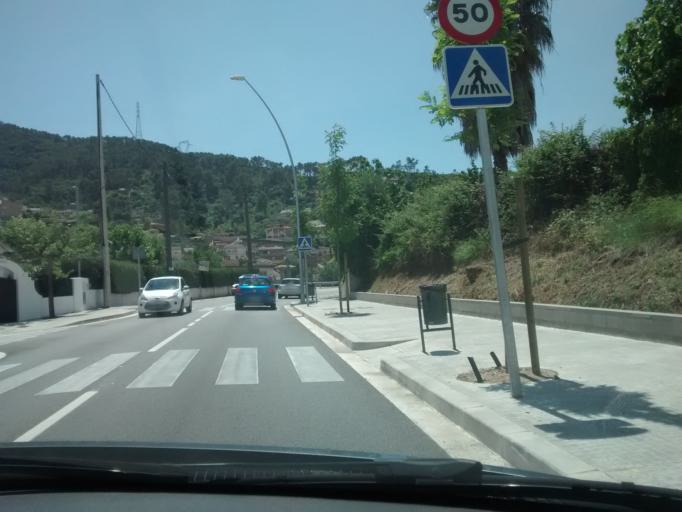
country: ES
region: Catalonia
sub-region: Provincia de Barcelona
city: Sant Vicenc dels Horts
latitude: 41.3810
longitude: 1.9965
